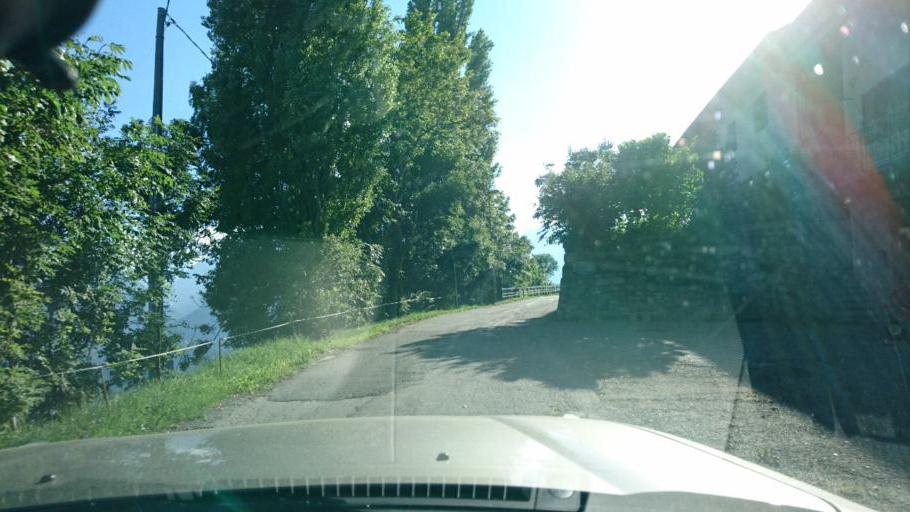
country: IT
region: Aosta Valley
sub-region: Valle d'Aosta
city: Villeneuve
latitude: 45.7202
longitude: 7.1955
